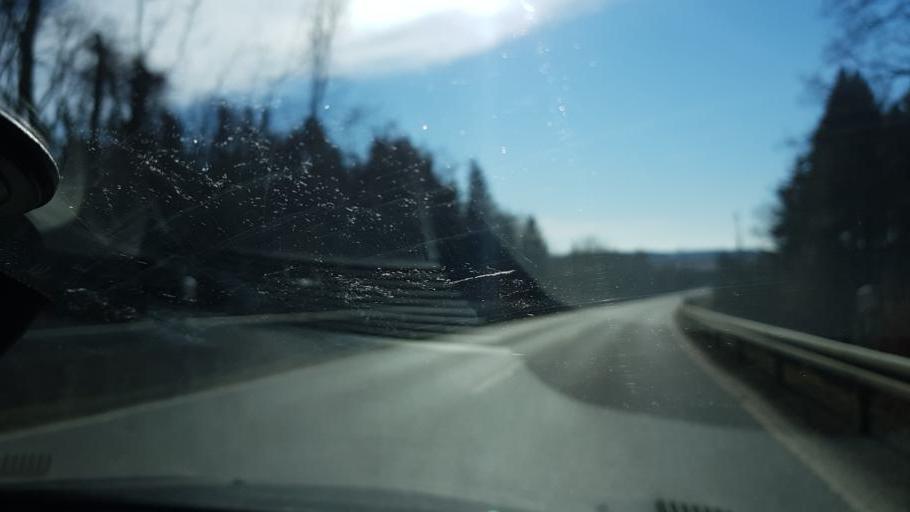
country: DE
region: Bavaria
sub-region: Upper Bavaria
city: Oberschweinbach
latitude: 48.2201
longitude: 11.1795
